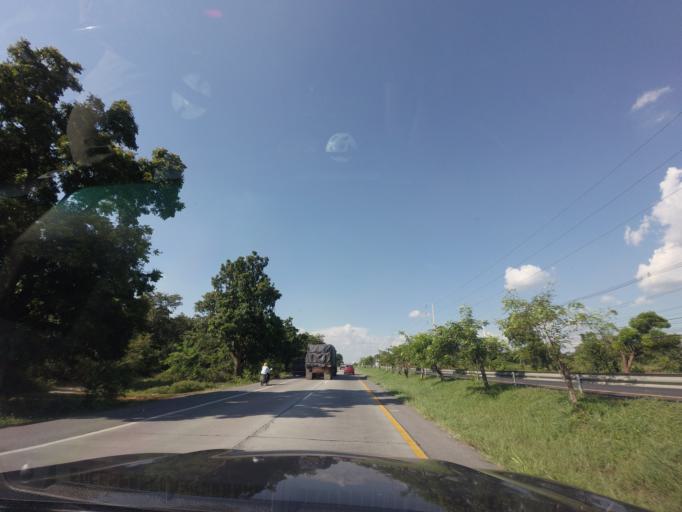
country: TH
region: Nakhon Ratchasima
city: Sida
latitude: 15.5607
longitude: 102.5513
